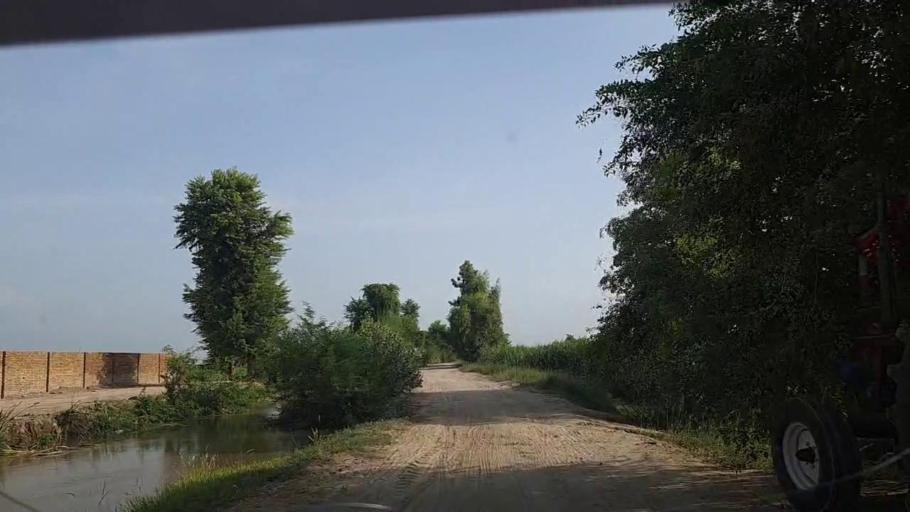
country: PK
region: Sindh
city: Ghotki
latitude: 28.0029
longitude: 69.2618
